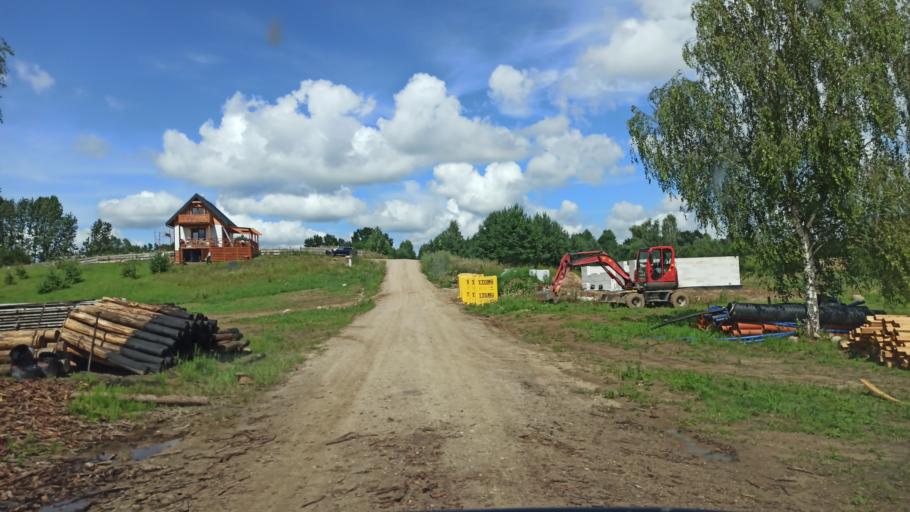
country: PL
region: Warmian-Masurian Voivodeship
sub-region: Powiat ostrodzki
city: Morag
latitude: 53.8546
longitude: 20.0668
